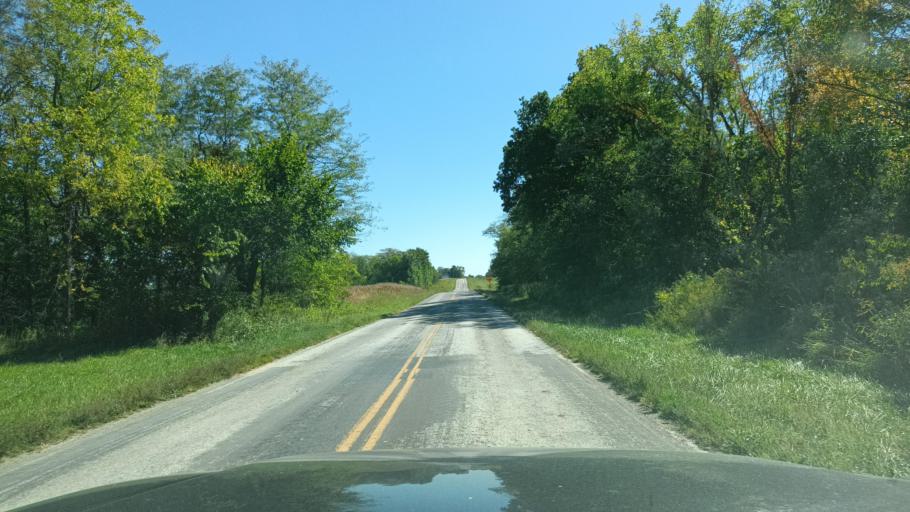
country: US
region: Missouri
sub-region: Macon County
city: La Plata
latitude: 40.0095
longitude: -92.5971
